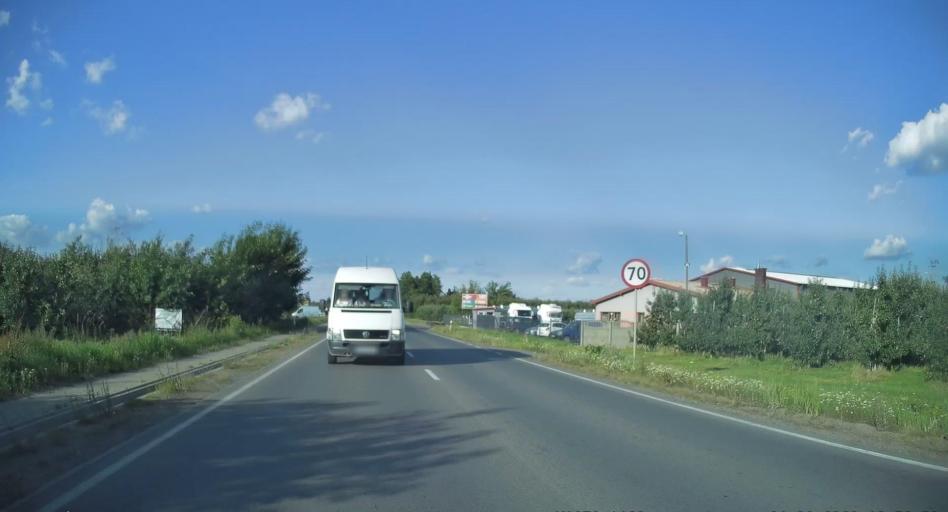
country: PL
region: Masovian Voivodeship
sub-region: Powiat grojecki
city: Belsk Duzy
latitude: 51.8429
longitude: 20.8312
